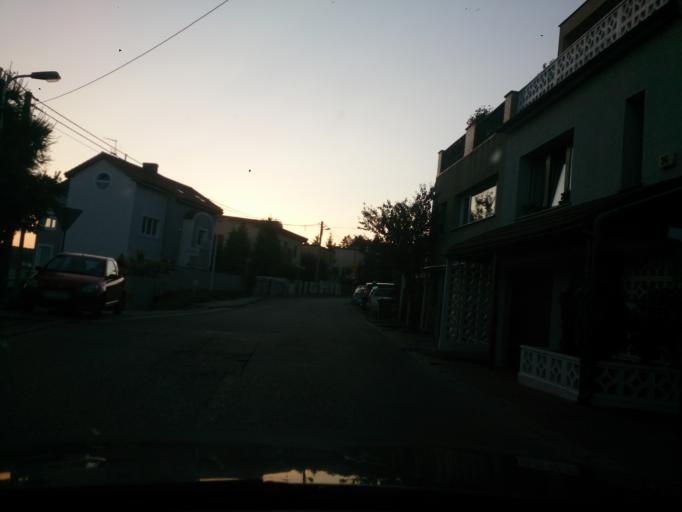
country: PL
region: Pomeranian Voivodeship
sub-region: Gdynia
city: Gdynia
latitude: 54.4904
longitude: 18.5535
